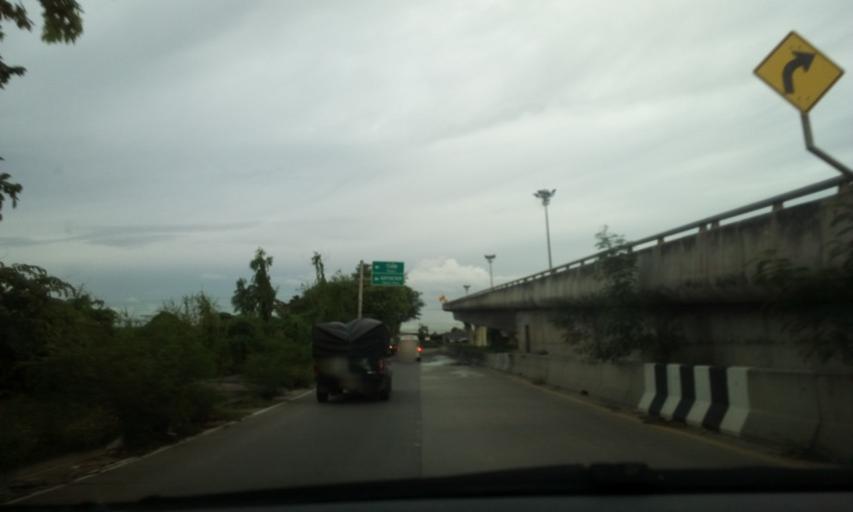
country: TH
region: Phra Nakhon Si Ayutthaya
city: Ban Bang Kadi Pathum Thani
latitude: 13.9705
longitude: 100.5539
